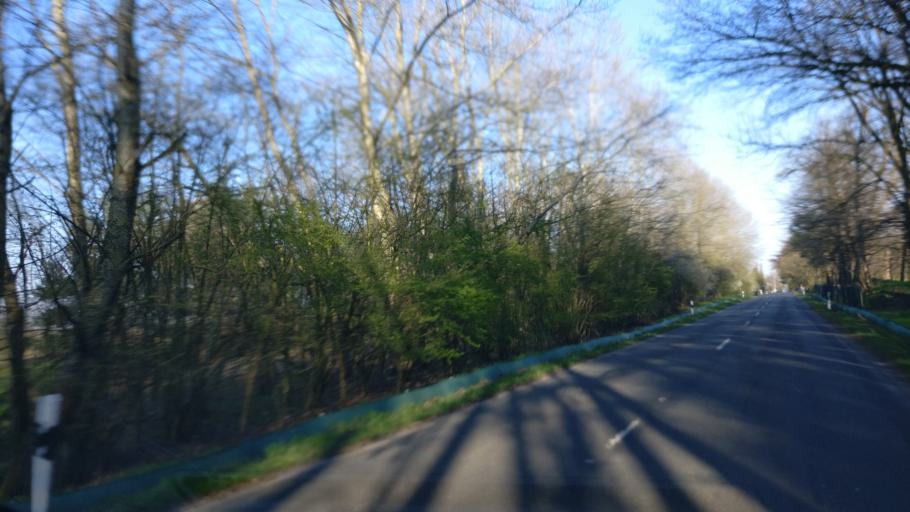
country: DE
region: North Rhine-Westphalia
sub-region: Regierungsbezirk Detmold
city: Lage
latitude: 52.0154
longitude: 8.7575
